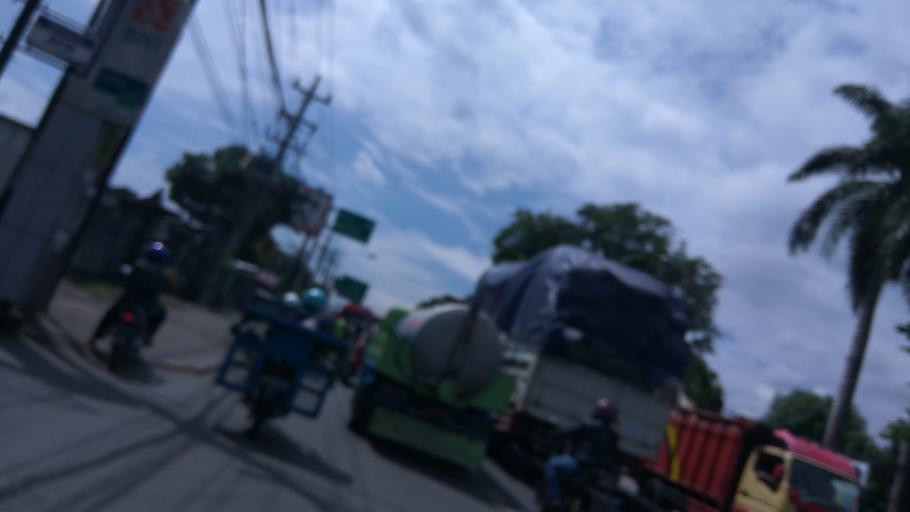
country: ID
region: Central Java
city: Ungaran
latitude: -7.1364
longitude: 110.4047
